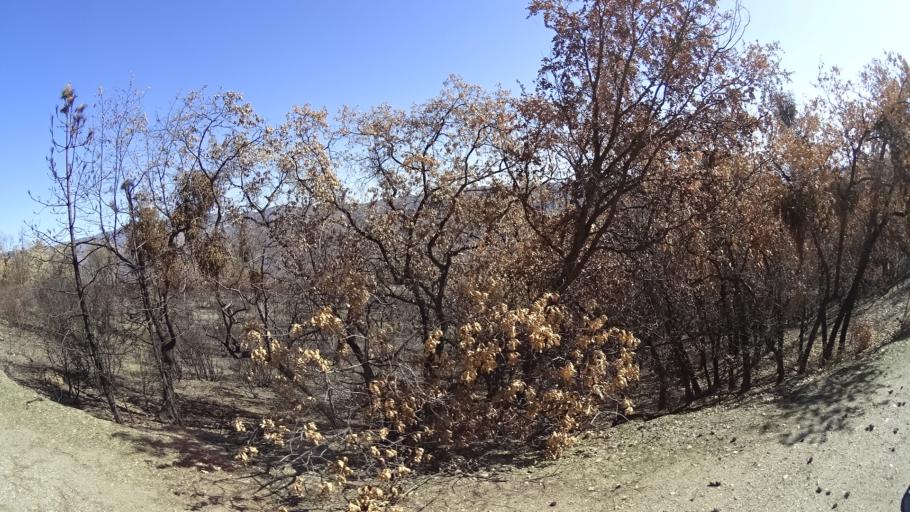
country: US
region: California
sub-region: Tehama County
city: Rancho Tehama Reserve
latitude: 39.6678
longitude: -122.6879
